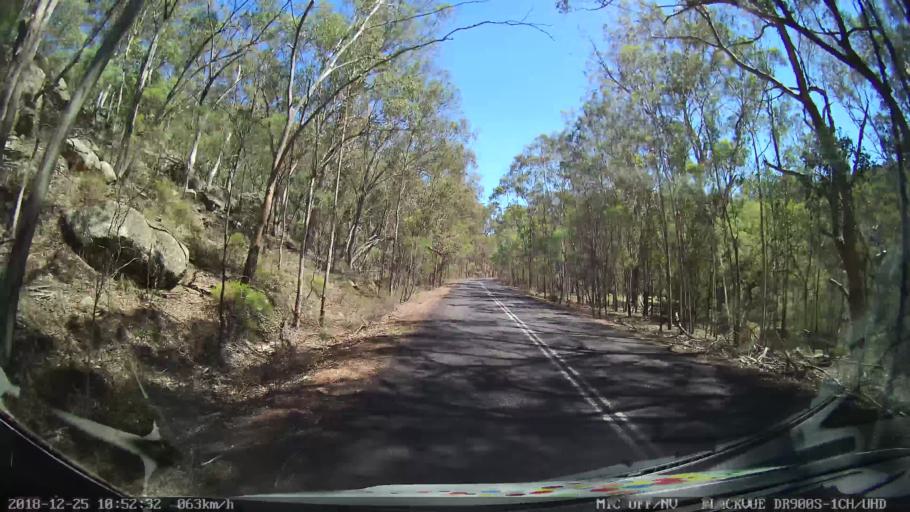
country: AU
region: New South Wales
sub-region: Upper Hunter Shire
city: Merriwa
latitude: -32.4278
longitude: 150.2734
